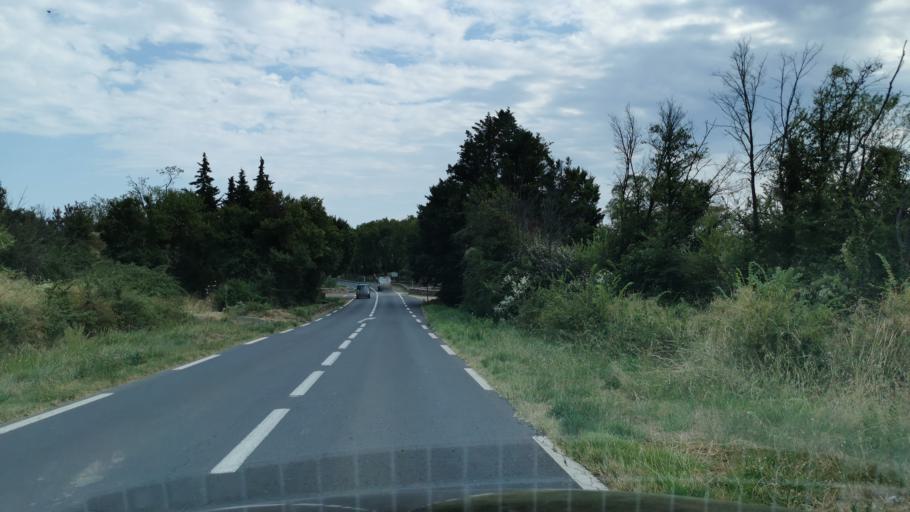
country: FR
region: Languedoc-Roussillon
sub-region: Departement de l'Herault
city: Capestang
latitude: 43.3417
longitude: 3.0397
